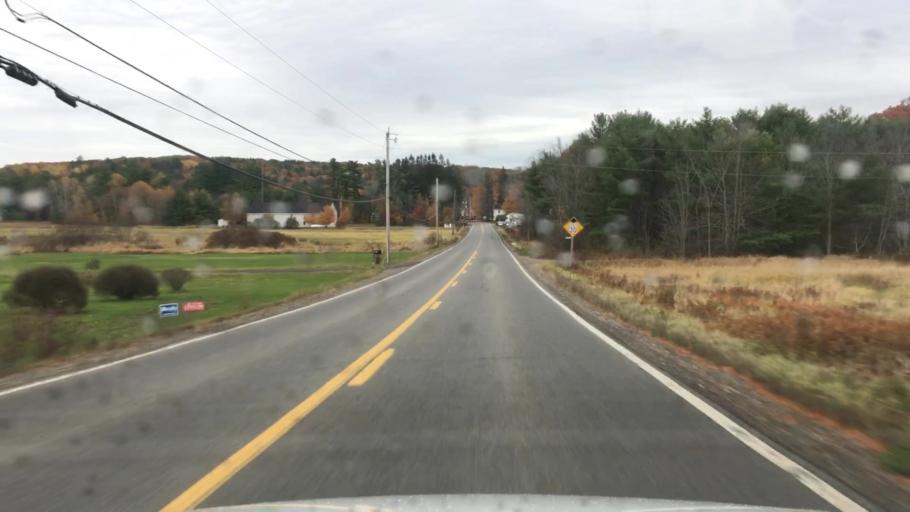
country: US
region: Maine
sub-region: Lincoln County
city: Jefferson
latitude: 44.2025
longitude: -69.4616
